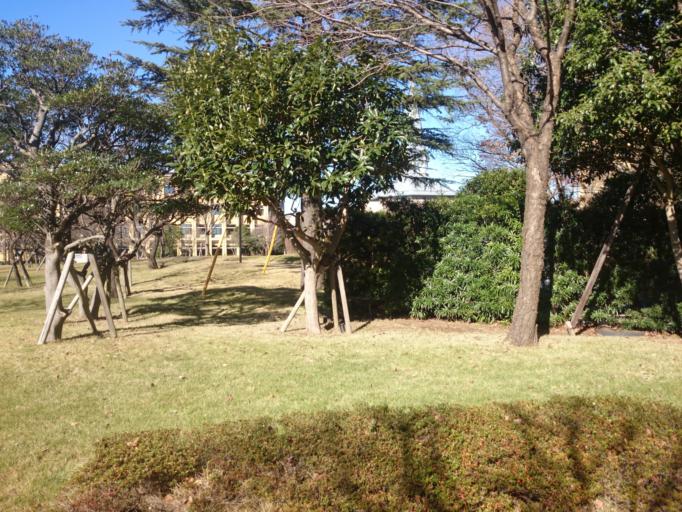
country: JP
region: Tokyo
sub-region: Machida-shi
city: Machida
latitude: 35.5652
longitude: 139.4023
